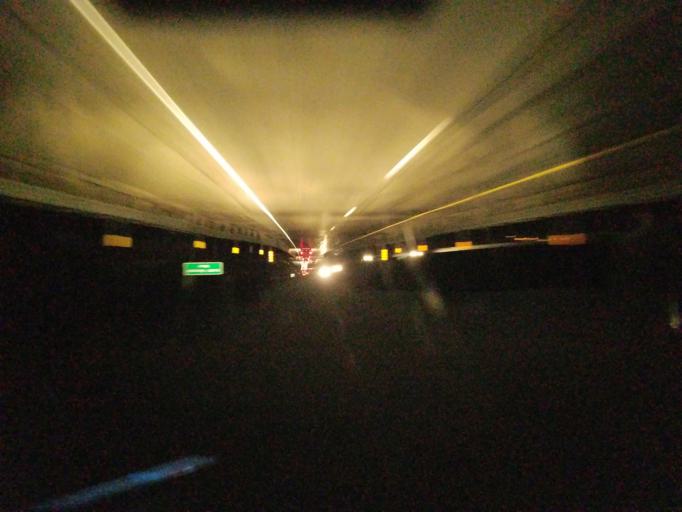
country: US
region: Iowa
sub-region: Dallas County
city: De Soto
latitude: 41.5430
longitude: -93.9856
